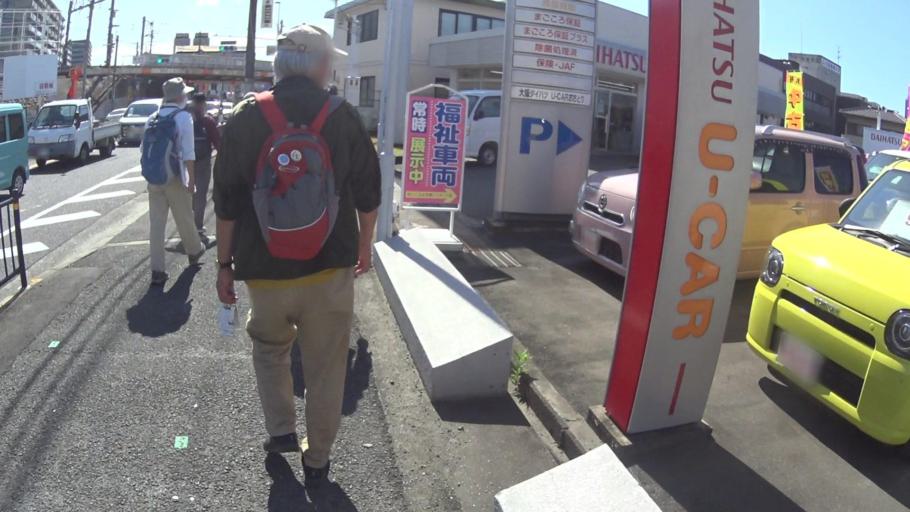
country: JP
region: Osaka
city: Sakai
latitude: 34.5354
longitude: 135.4878
